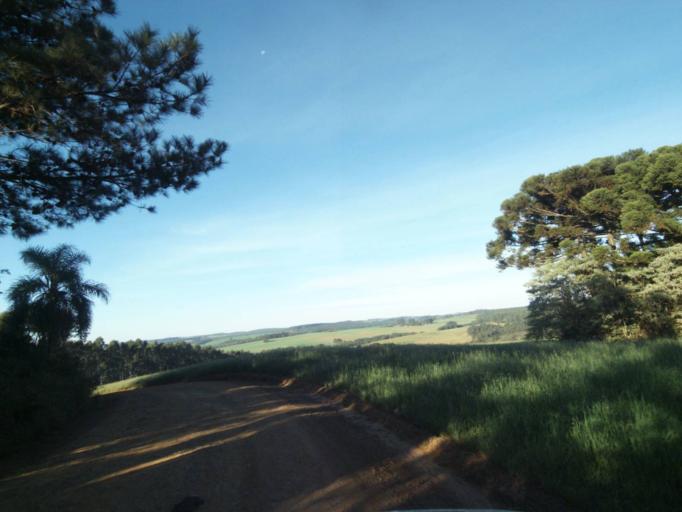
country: BR
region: Parana
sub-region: Tibagi
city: Tibagi
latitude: -24.5407
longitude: -50.6104
